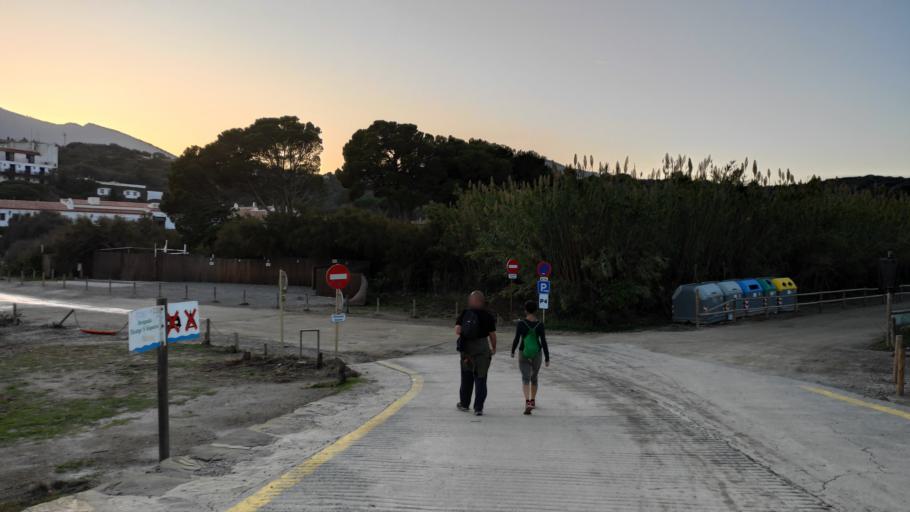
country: ES
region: Catalonia
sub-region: Provincia de Girona
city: Cadaques
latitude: 42.2946
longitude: 3.2876
